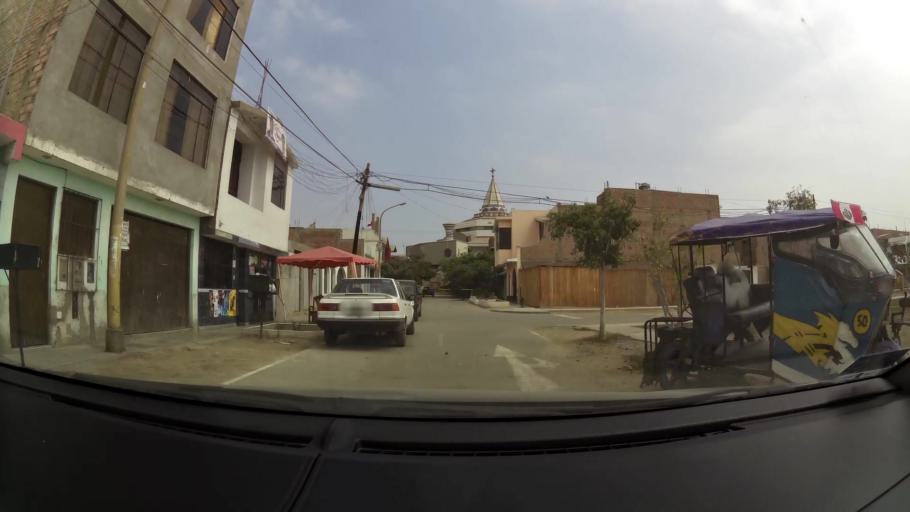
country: PE
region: Lima
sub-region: Lima
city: Santa Rosa
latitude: -11.7866
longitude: -77.1546
